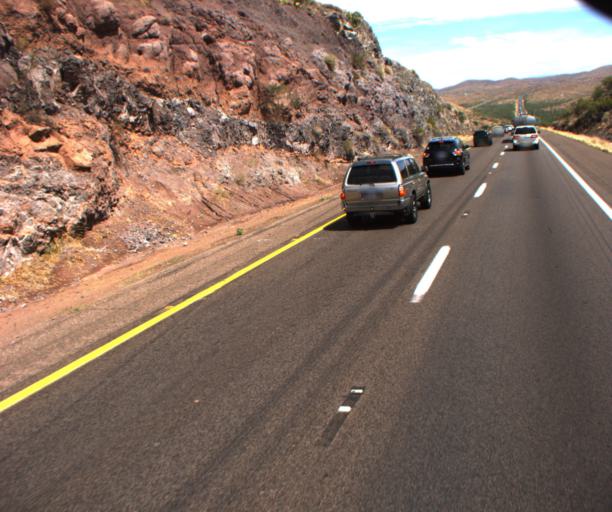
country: US
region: Arizona
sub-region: Yavapai County
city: Cordes Lakes
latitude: 34.2274
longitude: -112.1110
